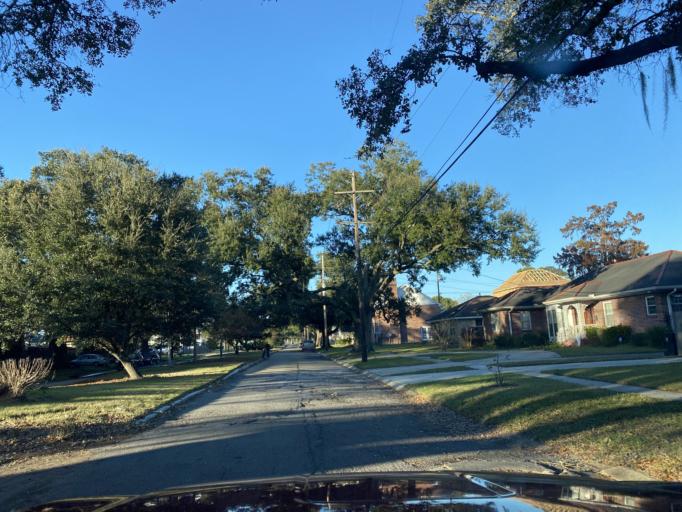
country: US
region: Louisiana
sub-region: Orleans Parish
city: New Orleans
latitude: 30.0110
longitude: -90.0556
